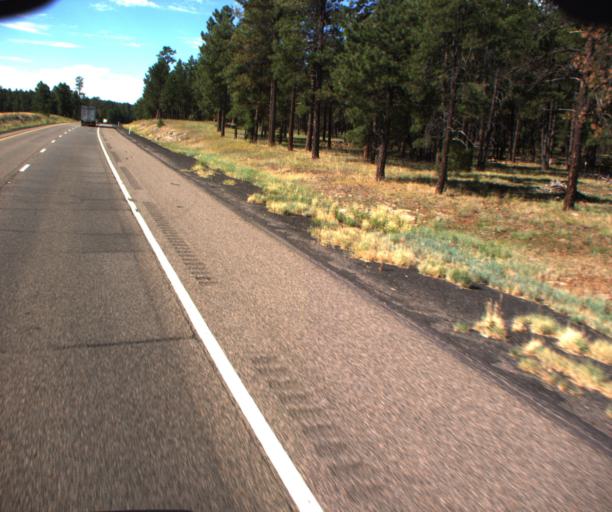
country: US
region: Arizona
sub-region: Coconino County
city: Sedona
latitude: 34.8388
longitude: -111.6045
